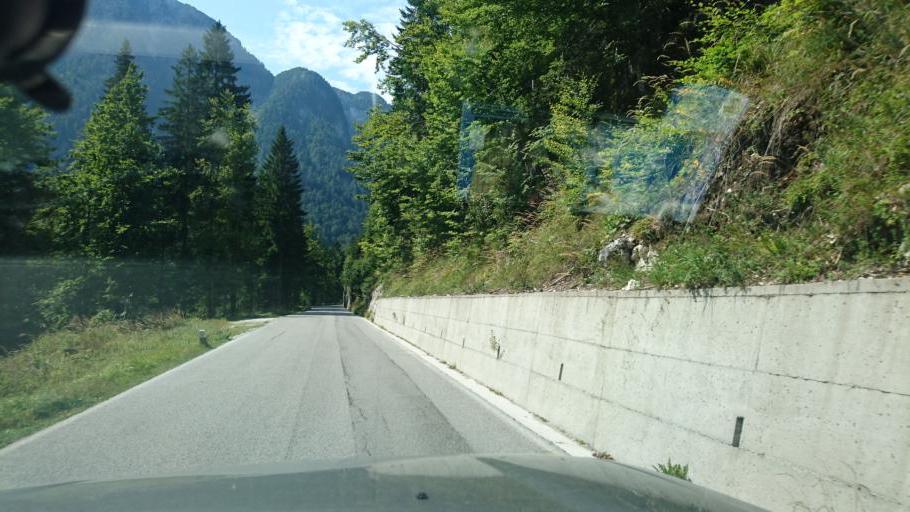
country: SI
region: Bovec
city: Bovec
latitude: 46.4071
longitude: 13.5319
